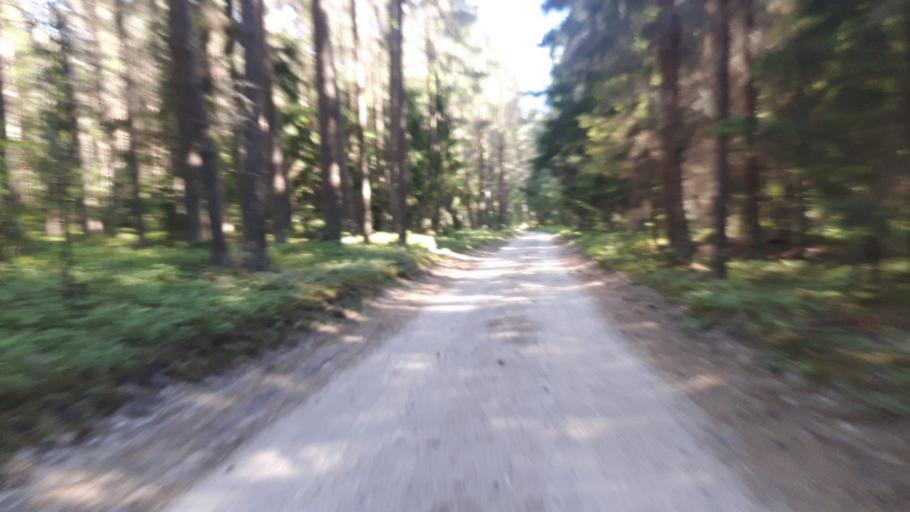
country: LV
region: Salacgrivas
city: Salacgriva
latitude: 57.7339
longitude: 24.3501
